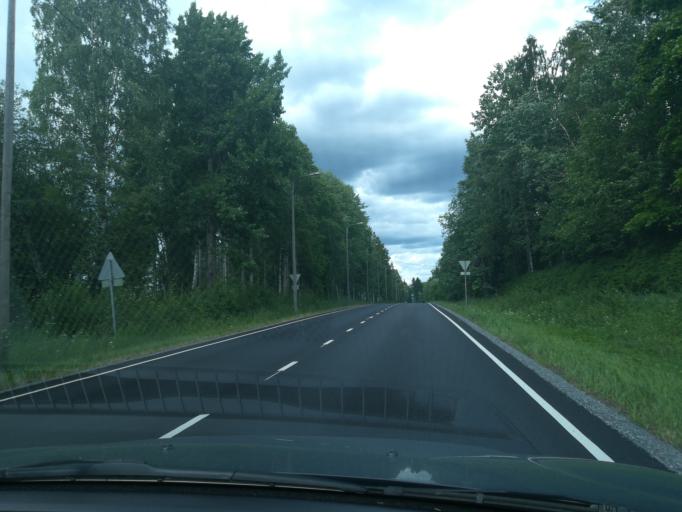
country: FI
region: Southern Savonia
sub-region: Mikkeli
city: Mikkeli
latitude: 61.6450
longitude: 27.0804
